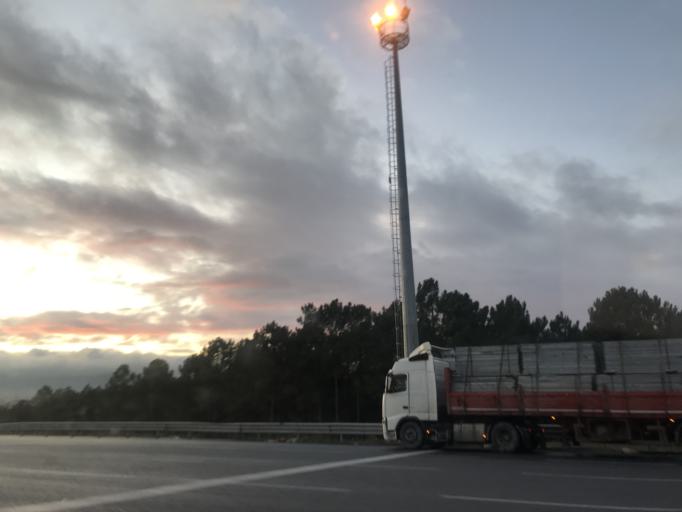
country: TR
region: Istanbul
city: Sultanbeyli
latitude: 40.9551
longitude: 29.3161
